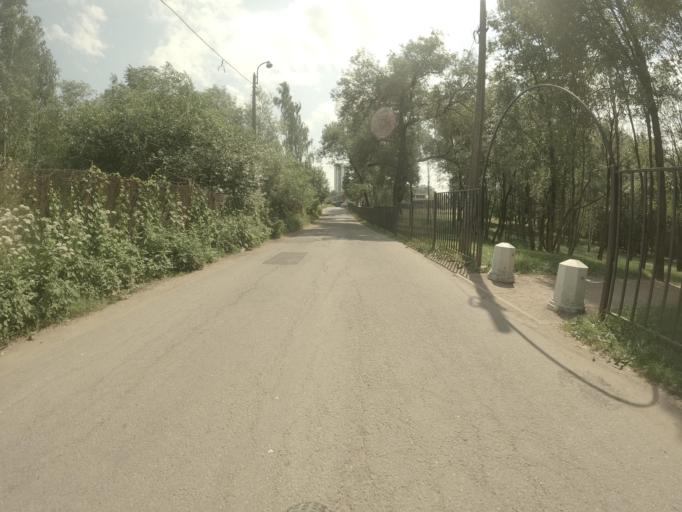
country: RU
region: St.-Petersburg
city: Krasnogvargeisky
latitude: 59.9635
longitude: 30.4731
